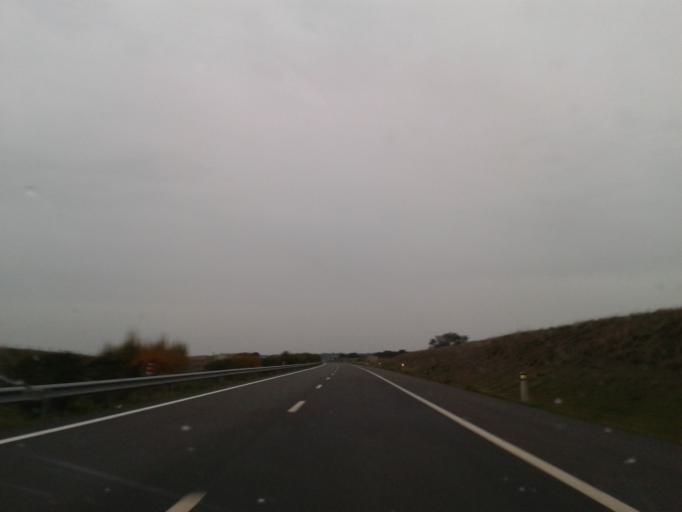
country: PT
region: Beja
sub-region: Aljustrel
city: Aljustrel
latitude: 37.9415
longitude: -8.2447
